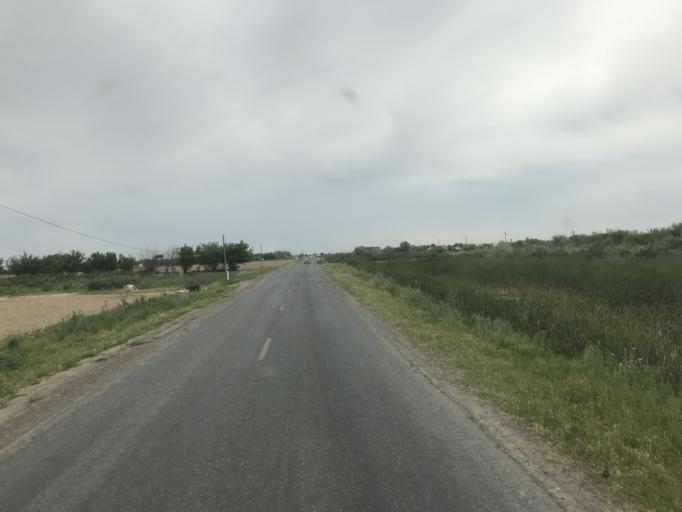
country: KZ
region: Ongtustik Qazaqstan
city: Asykata
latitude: 40.9208
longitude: 68.3999
